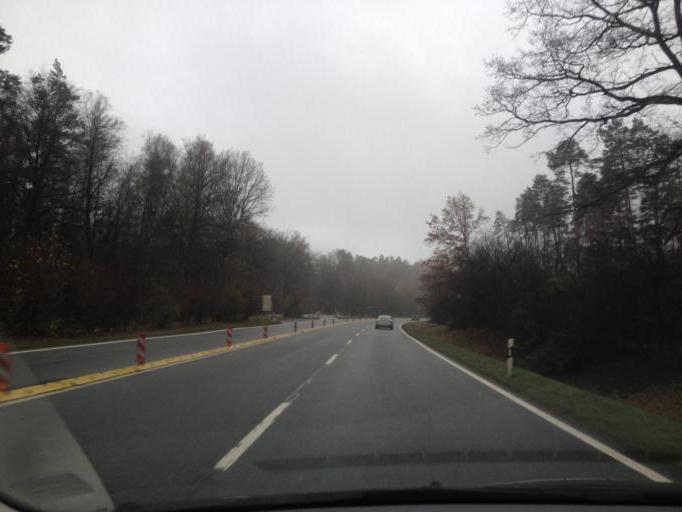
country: DE
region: Bavaria
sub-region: Regierungsbezirk Mittelfranken
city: Heroldsberg
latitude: 49.5183
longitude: 11.1467
